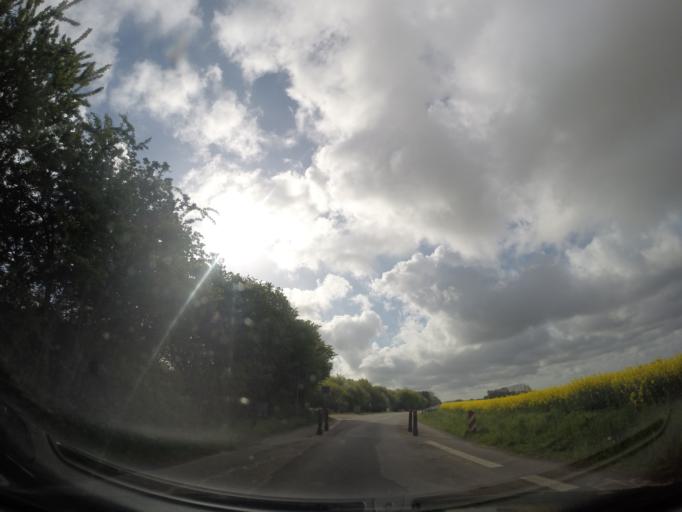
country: DK
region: Capital Region
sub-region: Hoje-Taastrup Kommune
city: Taastrup
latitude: 55.6853
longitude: 12.2942
